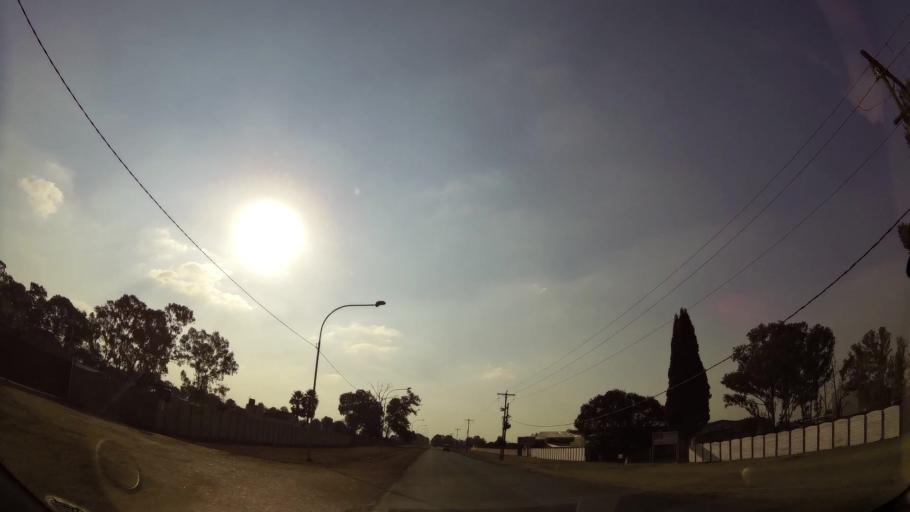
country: ZA
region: Gauteng
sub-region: Ekurhuleni Metropolitan Municipality
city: Benoni
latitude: -26.1191
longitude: 28.3907
